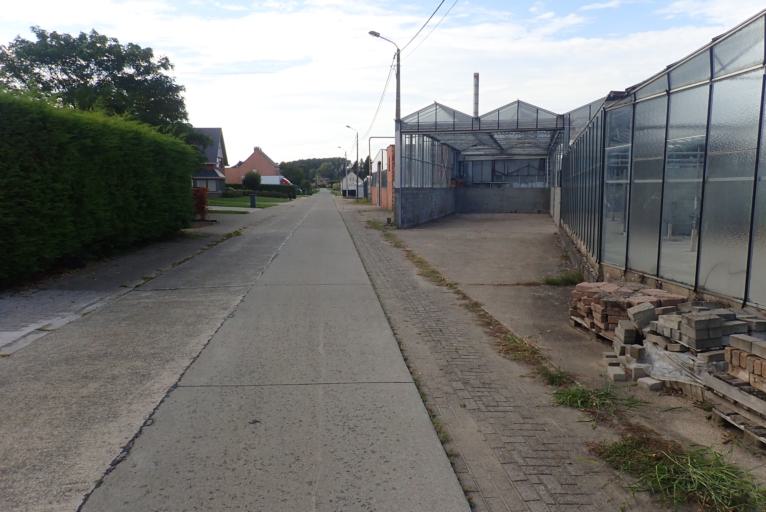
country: BE
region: Flanders
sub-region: Provincie Antwerpen
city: Duffel
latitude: 51.0786
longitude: 4.5099
